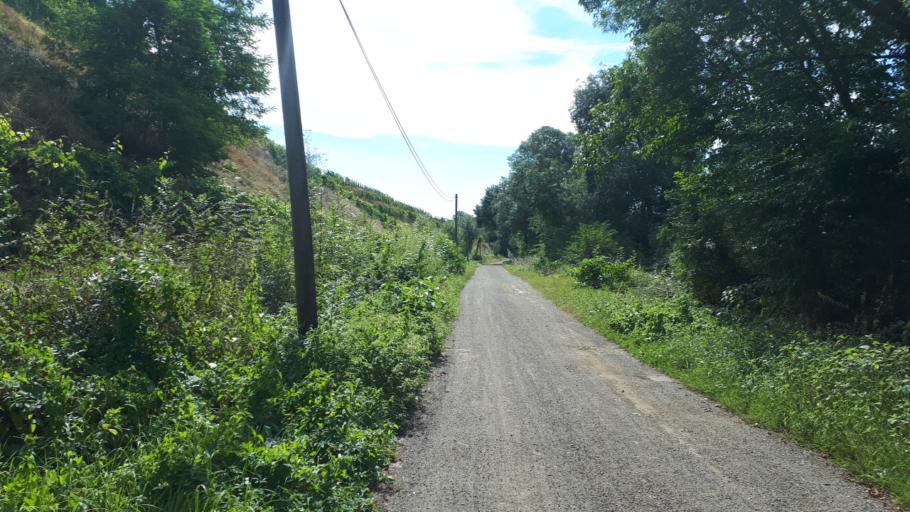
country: FR
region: Pays de la Loire
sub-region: Departement de Maine-et-Loire
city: Saint-Lambert-du-Lattay
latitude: 47.3224
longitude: -0.6544
